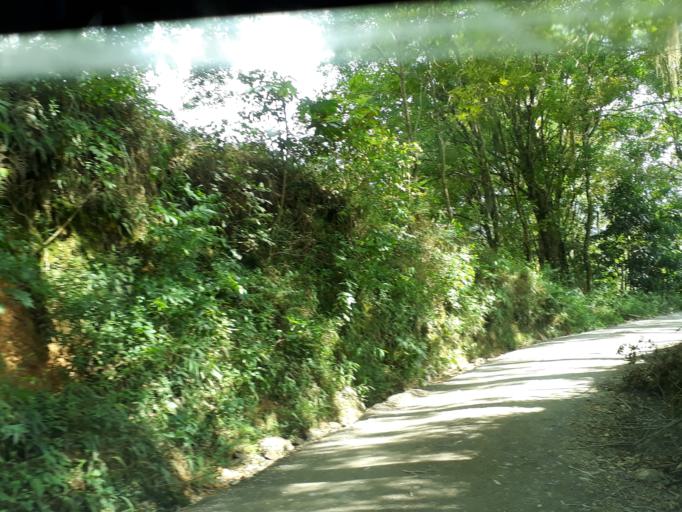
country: CO
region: Cundinamarca
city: Pacho
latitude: 5.2205
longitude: -74.1879
